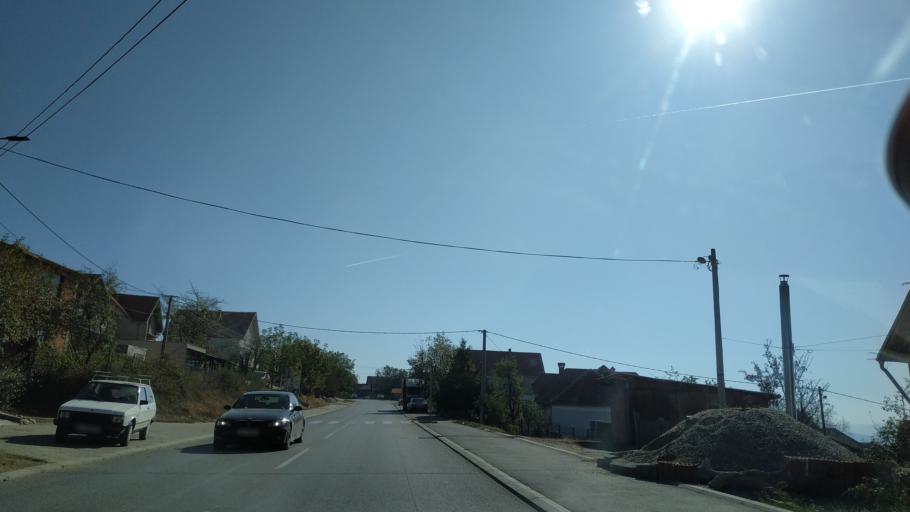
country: RS
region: Central Serbia
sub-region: Nisavski Okrug
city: Aleksinac
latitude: 43.5484
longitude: 21.6926
